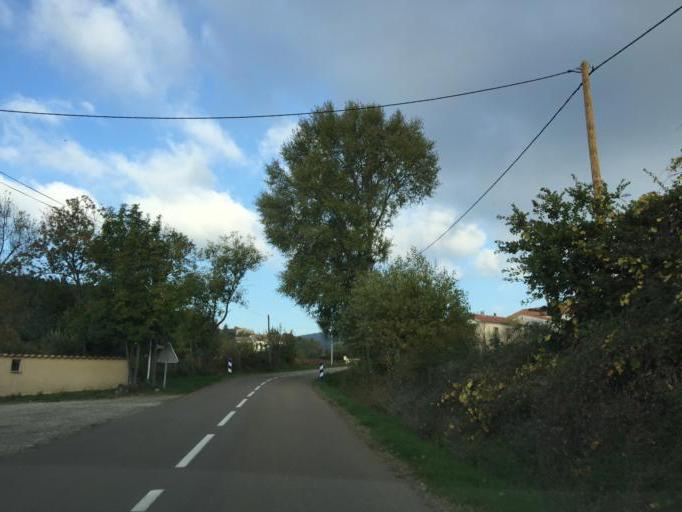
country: FR
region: Rhone-Alpes
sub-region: Departement de l'Ardeche
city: Bourg-Saint-Andeol
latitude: 44.4309
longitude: 4.6455
